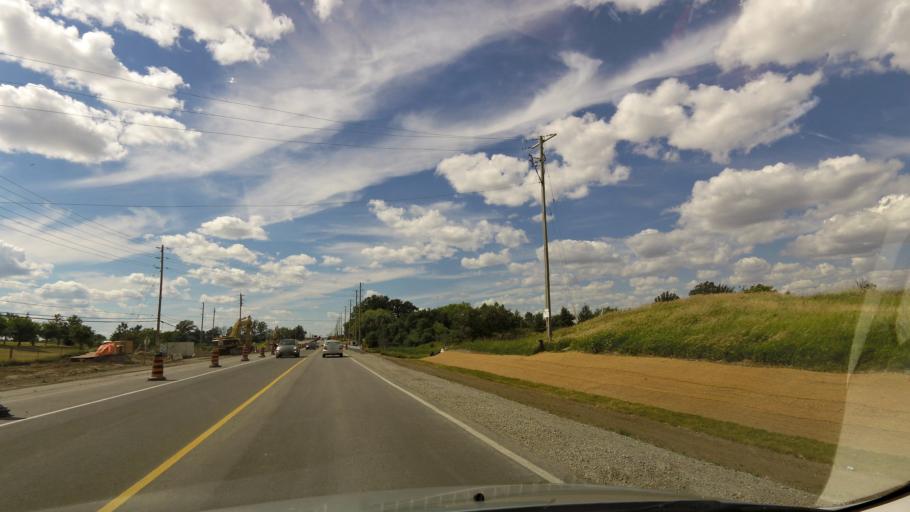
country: CA
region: Ontario
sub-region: Halton
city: Milton
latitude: 43.4779
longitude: -79.8224
